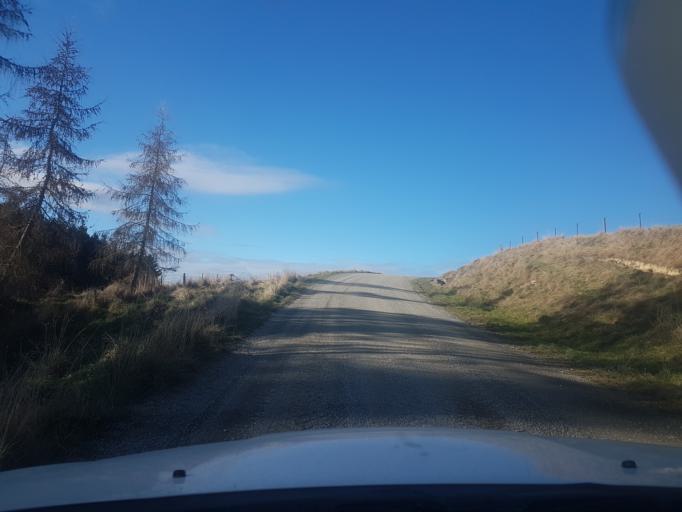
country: NZ
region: Canterbury
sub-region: Timaru District
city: Pleasant Point
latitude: -44.1669
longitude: 170.9141
